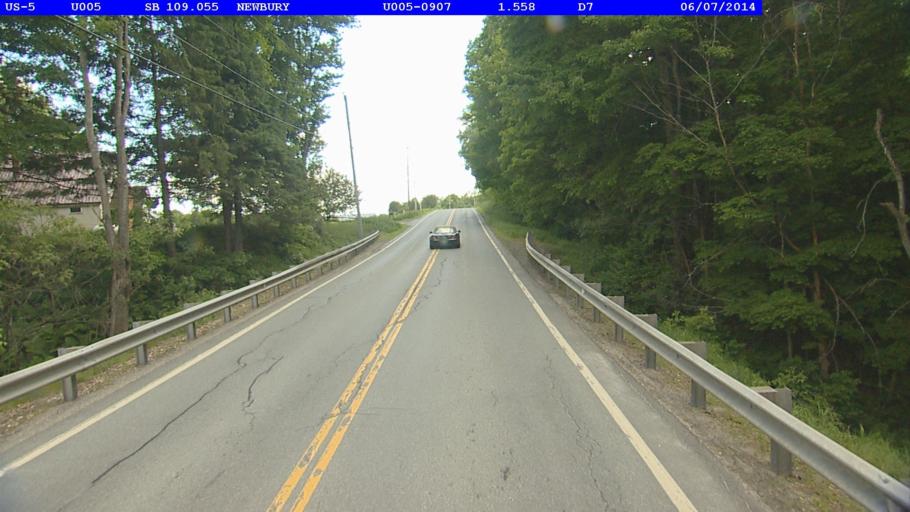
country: US
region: New Hampshire
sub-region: Grafton County
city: Haverhill
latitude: 44.0515
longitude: -72.0742
